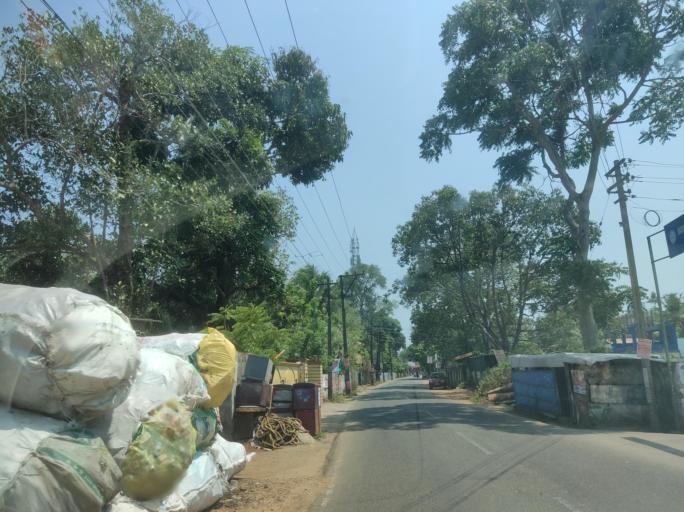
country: IN
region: Kerala
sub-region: Alappuzha
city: Kutiatodu
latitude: 9.7765
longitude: 76.3052
